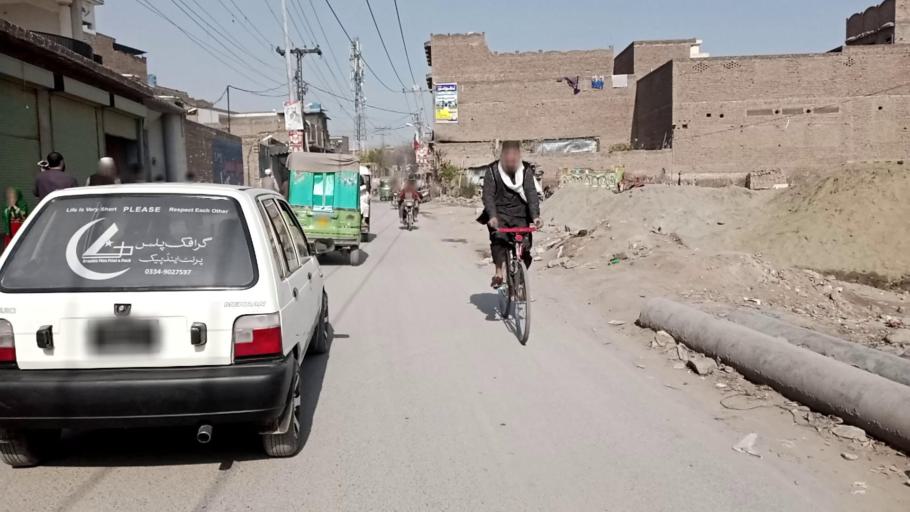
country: PK
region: Khyber Pakhtunkhwa
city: Peshawar
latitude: 33.9944
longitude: 71.5789
